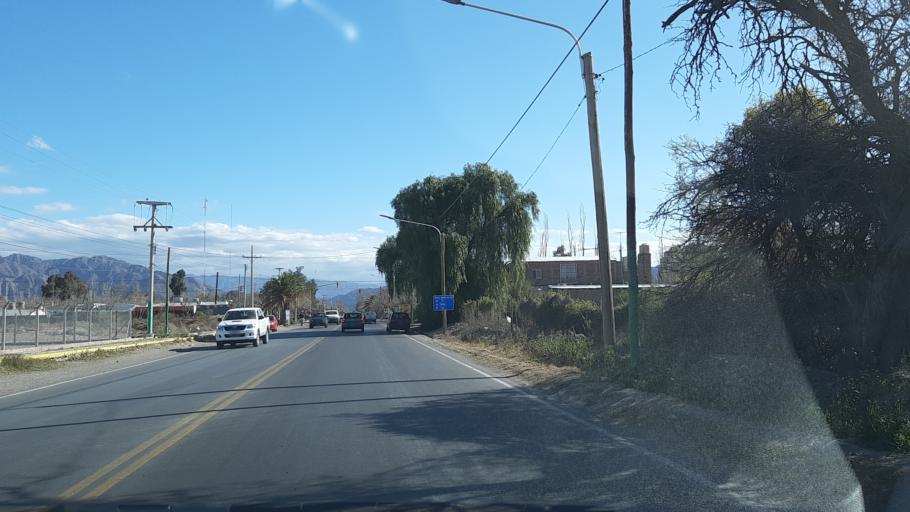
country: AR
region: San Juan
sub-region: Departamento de Rivadavia
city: Rivadavia
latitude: -31.5394
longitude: -68.6145
